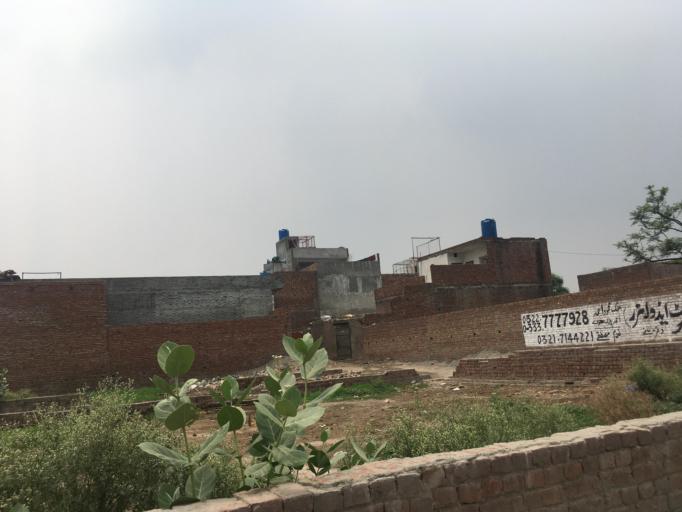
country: PK
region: Punjab
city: Lahore
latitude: 31.6169
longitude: 74.3552
